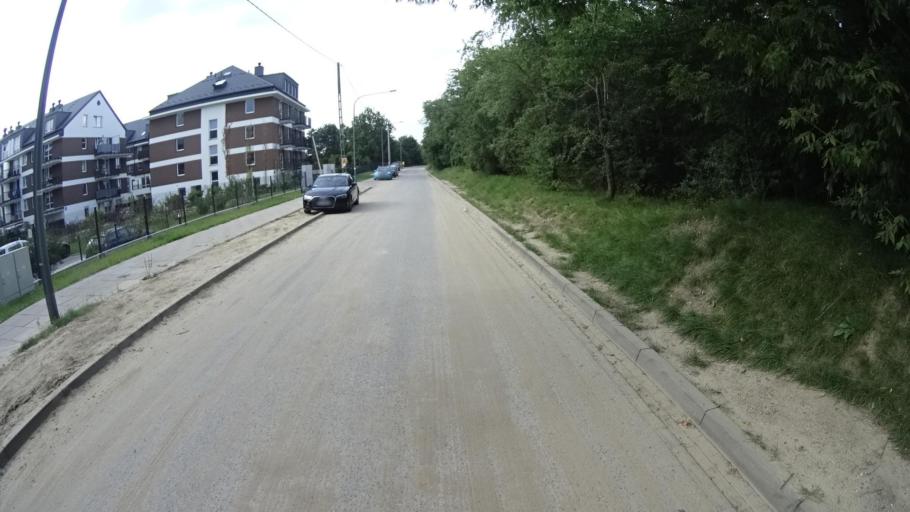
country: PL
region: Masovian Voivodeship
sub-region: Warszawa
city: Ursus
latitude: 52.2204
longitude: 20.8899
